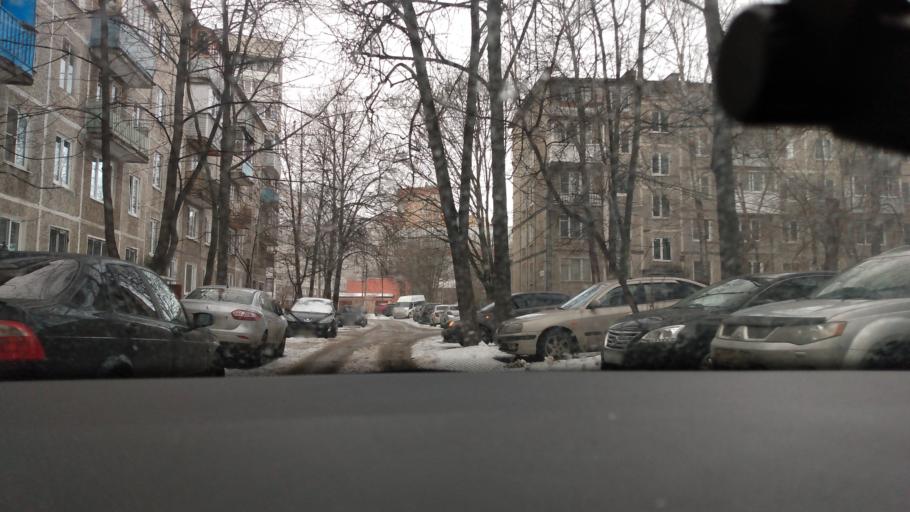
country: RU
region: Moskovskaya
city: Shchelkovo
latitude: 55.9178
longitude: 37.9907
